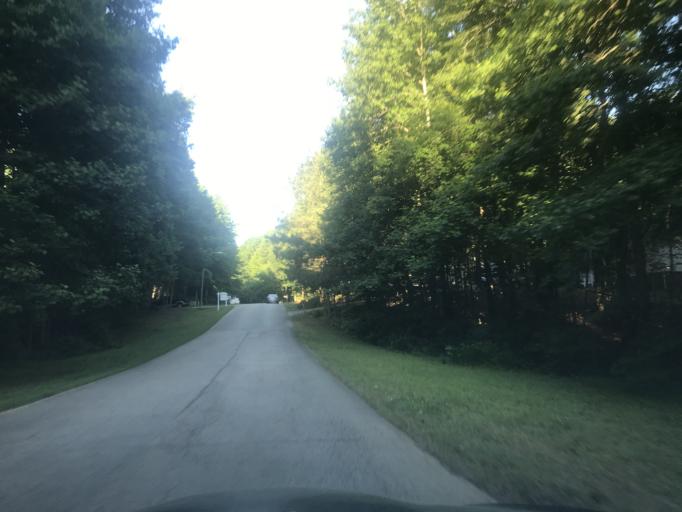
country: US
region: North Carolina
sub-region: Johnston County
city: Archer Lodge
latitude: 35.6818
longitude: -78.3533
